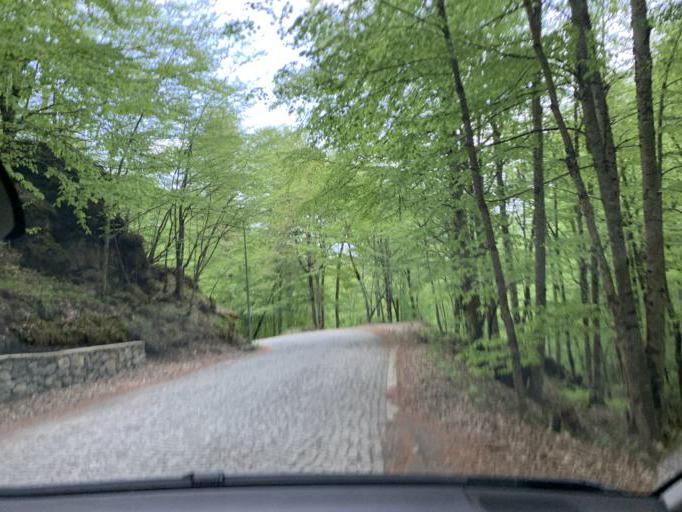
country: TR
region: Zonguldak
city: Egerci
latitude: 40.9355
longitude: 31.7412
